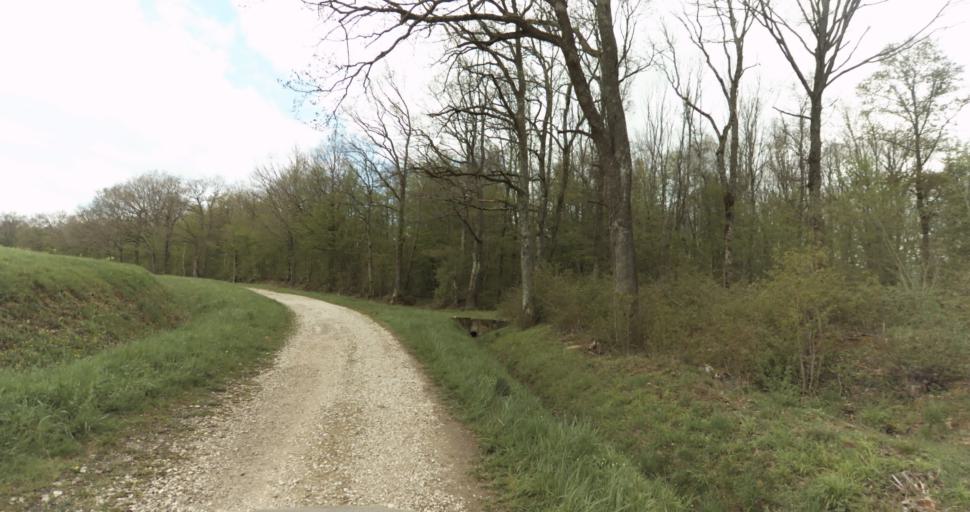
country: FR
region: Franche-Comte
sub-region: Departement du Jura
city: Champvans
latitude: 47.1496
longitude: 5.4252
